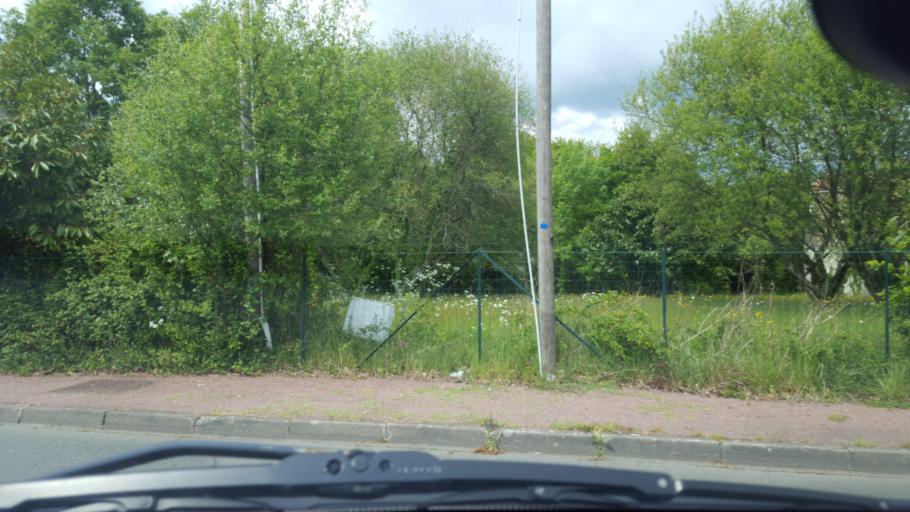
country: FR
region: Pays de la Loire
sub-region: Departement de la Loire-Atlantique
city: Saint-Philbert-de-Grand-Lieu
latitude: 47.0353
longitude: -1.6336
